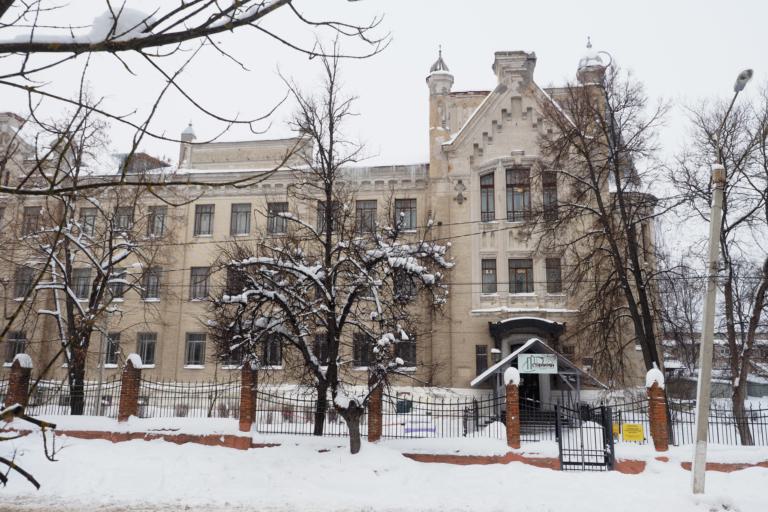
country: RU
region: Moskovskaya
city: Yegor'yevsk
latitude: 55.3823
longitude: 39.0210
